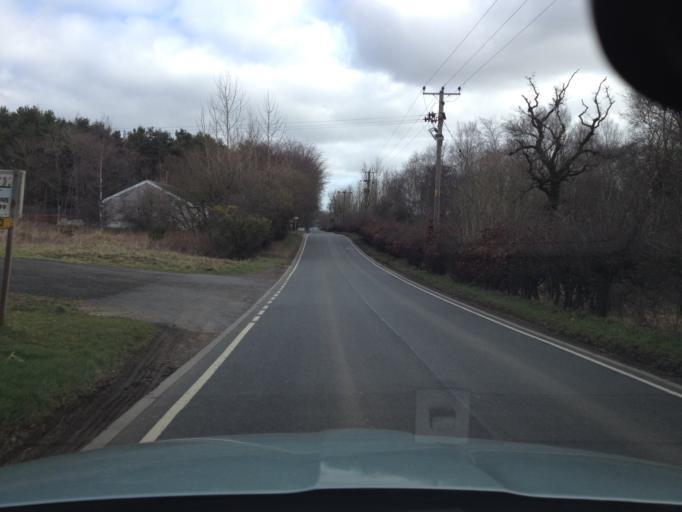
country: GB
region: Scotland
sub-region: West Lothian
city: Broxburn
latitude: 55.9150
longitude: -3.4678
